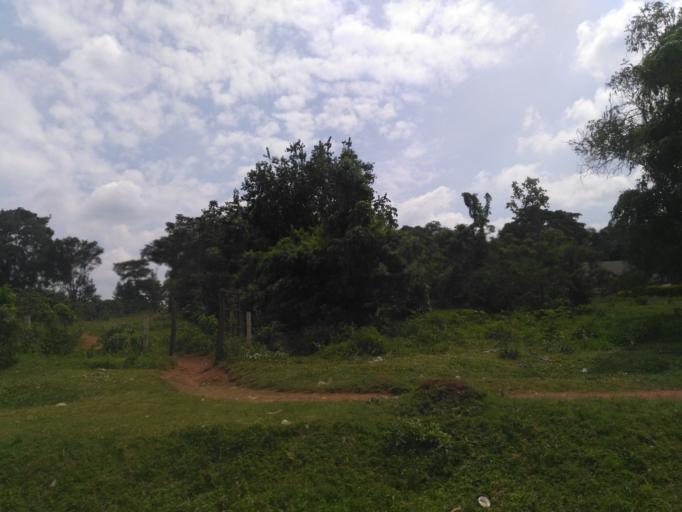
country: UG
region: Central Region
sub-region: Wakiso District
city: Kireka
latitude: 0.4629
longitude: 32.6057
